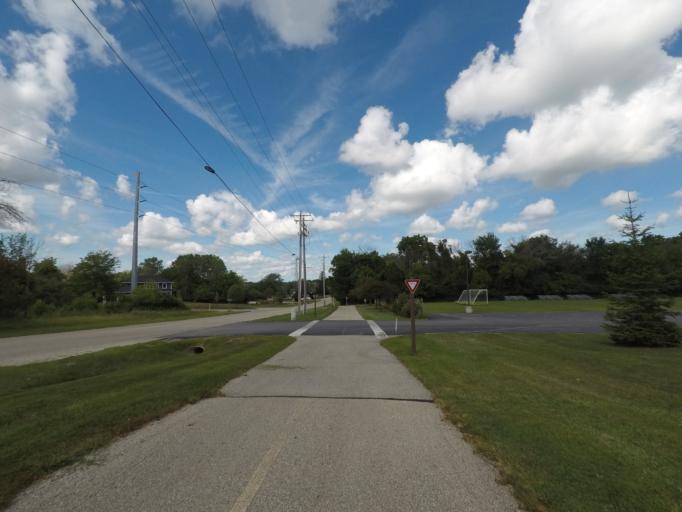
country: US
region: Wisconsin
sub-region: Waukesha County
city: Pewaukee
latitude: 43.0573
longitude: -88.3060
